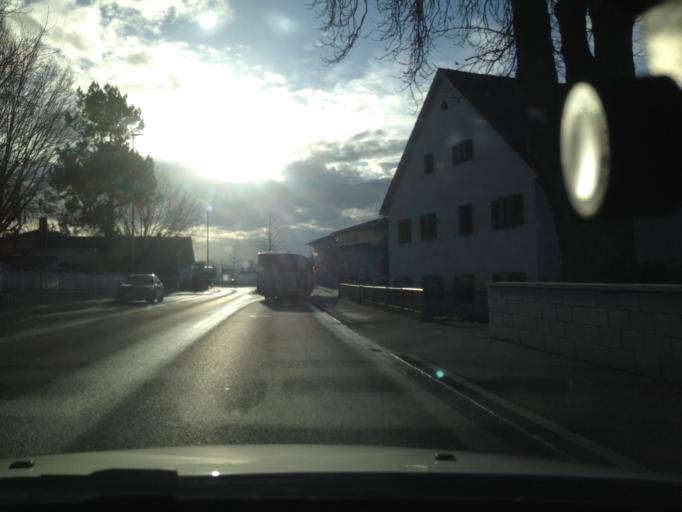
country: DE
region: Bavaria
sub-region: Swabia
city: Grossaitingen
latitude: 48.2226
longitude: 10.7782
